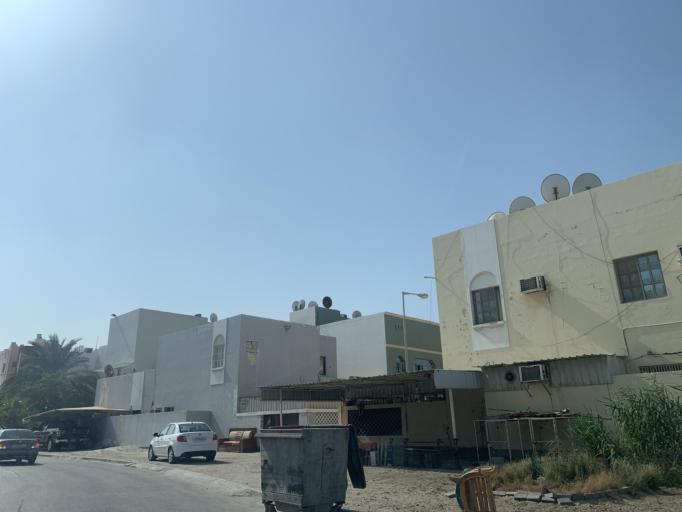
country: BH
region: Central Governorate
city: Madinat Hamad
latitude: 26.1290
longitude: 50.5013
